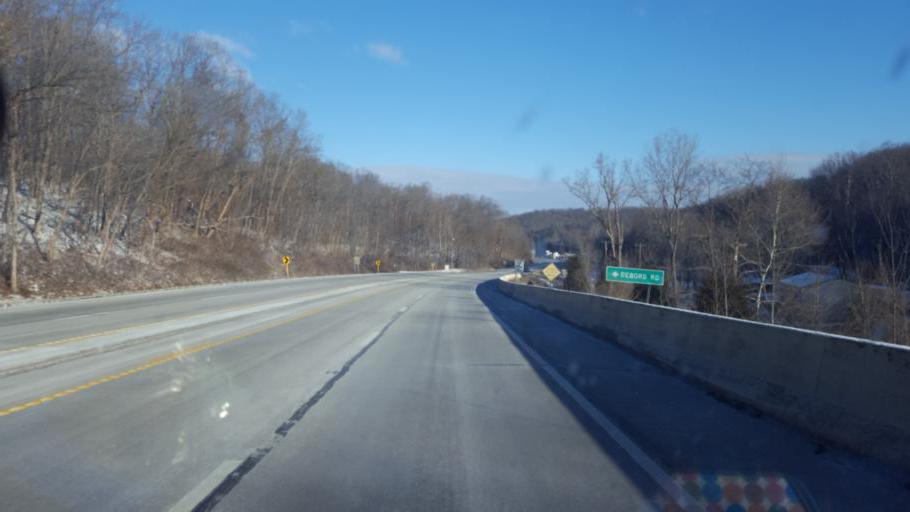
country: US
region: Ohio
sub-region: Pike County
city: Waverly
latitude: 39.2205
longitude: -82.9841
